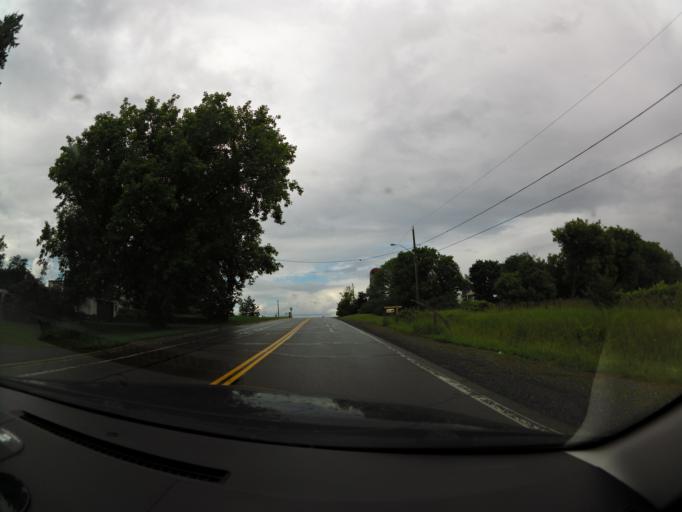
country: CA
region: Ontario
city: Perth
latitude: 45.0816
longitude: -76.4417
